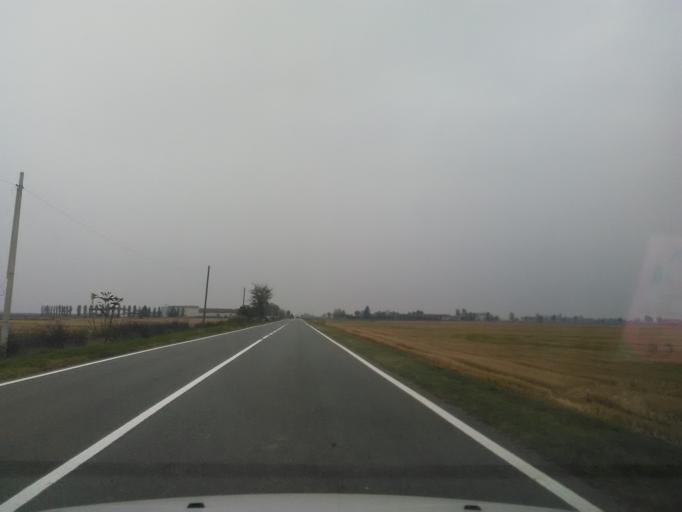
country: IT
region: Piedmont
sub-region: Provincia di Vercelli
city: Ronsecco
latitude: 45.2613
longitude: 8.2366
